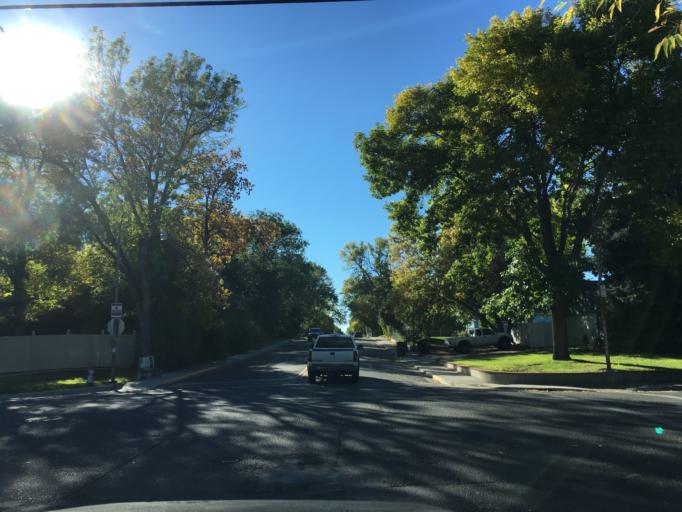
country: US
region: Montana
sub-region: Yellowstone County
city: Billings
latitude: 45.7899
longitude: -108.5277
